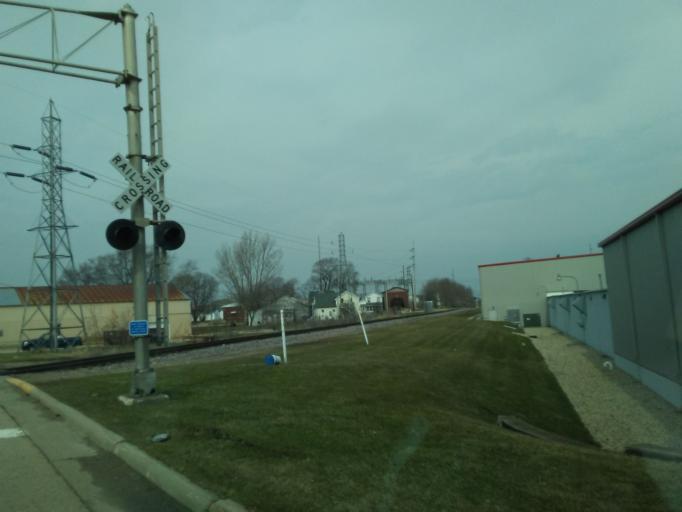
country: US
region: Wisconsin
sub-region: Columbia County
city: Lodi
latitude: 43.2505
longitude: -89.4989
